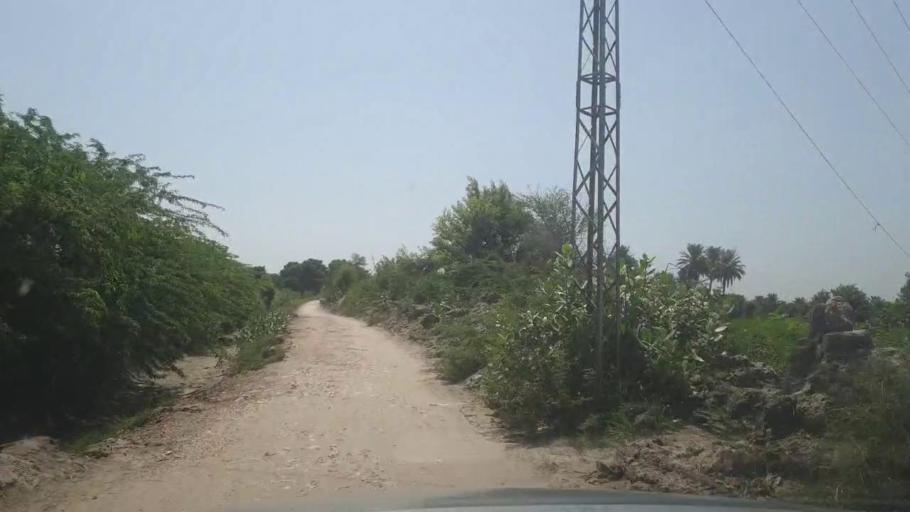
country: PK
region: Sindh
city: Khairpur
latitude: 27.3608
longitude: 69.0321
